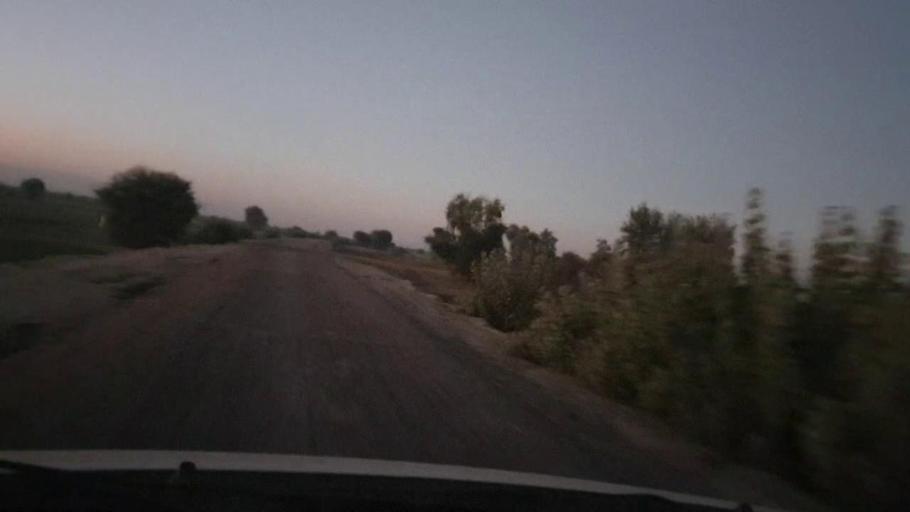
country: PK
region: Sindh
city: Phulji
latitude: 26.9017
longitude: 67.4713
